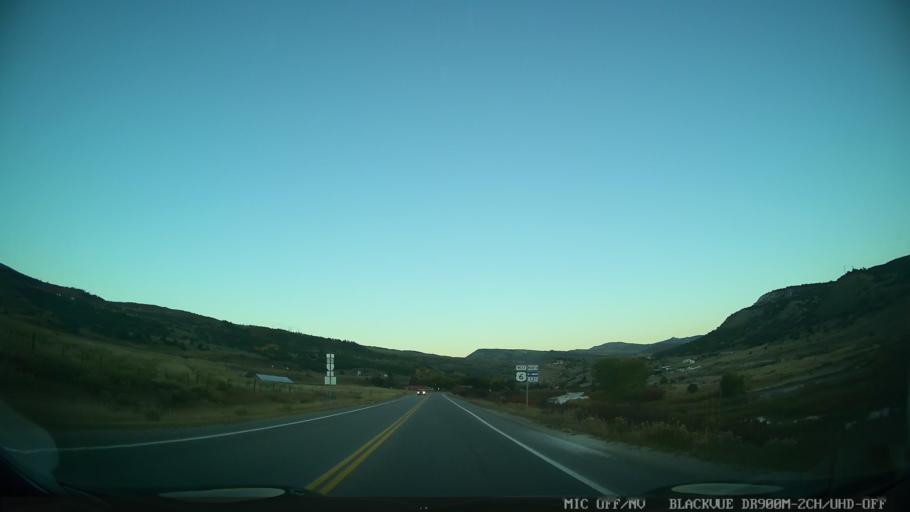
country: US
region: Colorado
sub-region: Eagle County
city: Edwards
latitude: 39.7004
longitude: -106.6704
